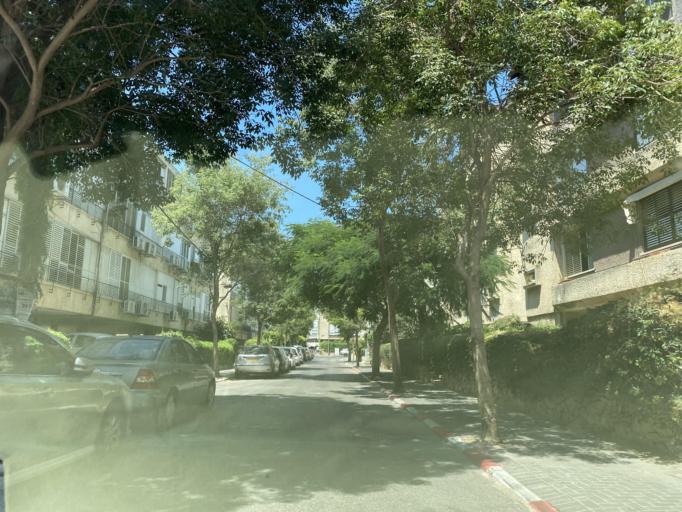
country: IL
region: Tel Aviv
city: Herzliyya
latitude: 32.1656
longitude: 34.8438
